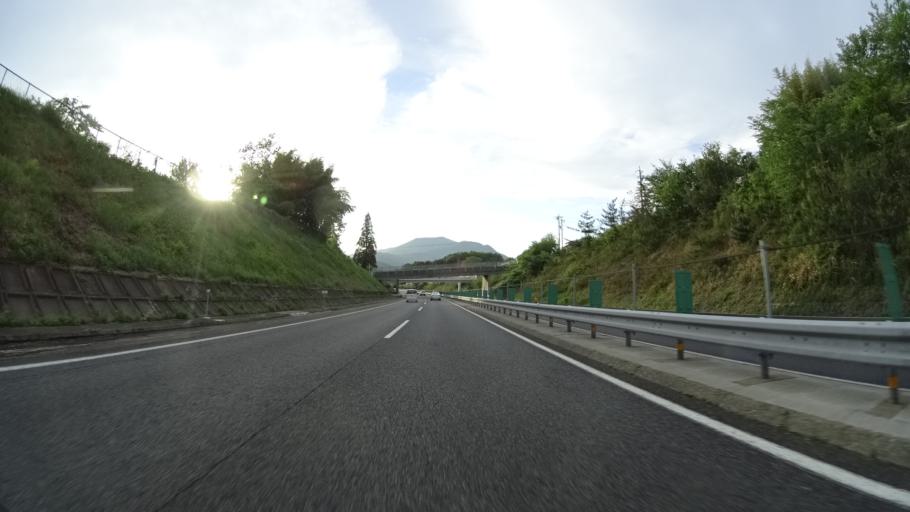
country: JP
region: Gifu
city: Nakatsugawa
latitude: 35.4572
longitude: 137.4187
